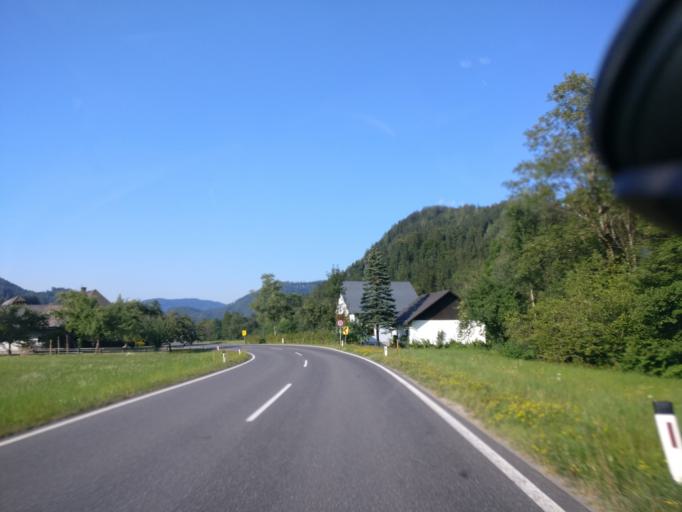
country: AT
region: Lower Austria
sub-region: Politischer Bezirk Scheibbs
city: Gostling an der Ybbs
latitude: 47.7834
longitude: 14.9145
